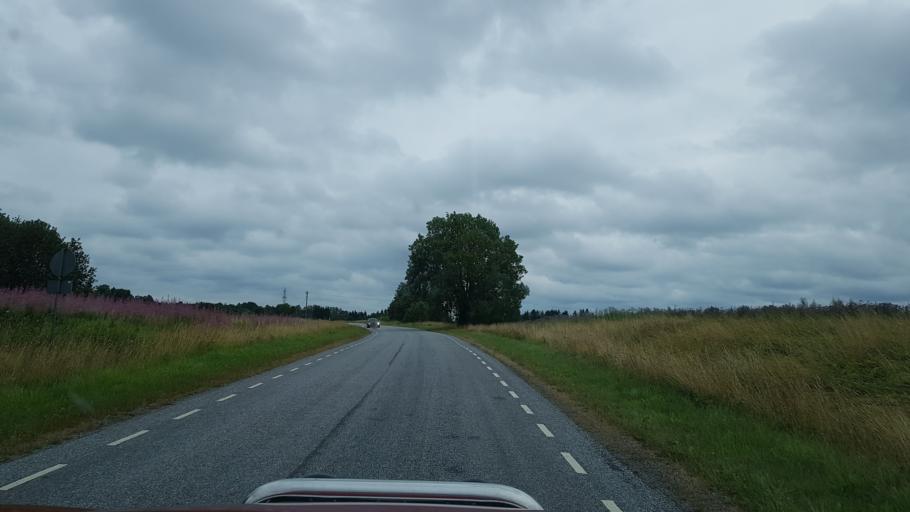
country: EE
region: Ida-Virumaa
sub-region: Puessi linn
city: Pussi
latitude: 59.3770
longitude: 27.0381
